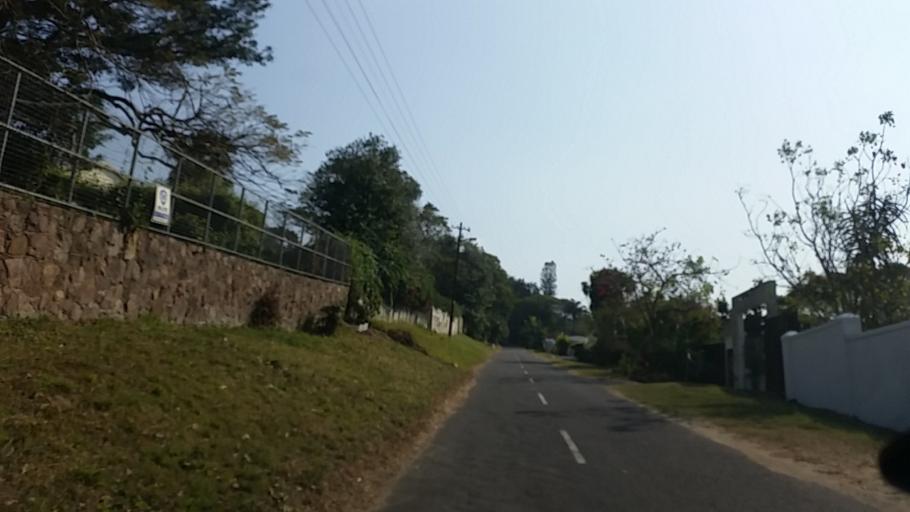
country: ZA
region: KwaZulu-Natal
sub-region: eThekwini Metropolitan Municipality
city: Berea
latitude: -29.8391
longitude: 30.9393
